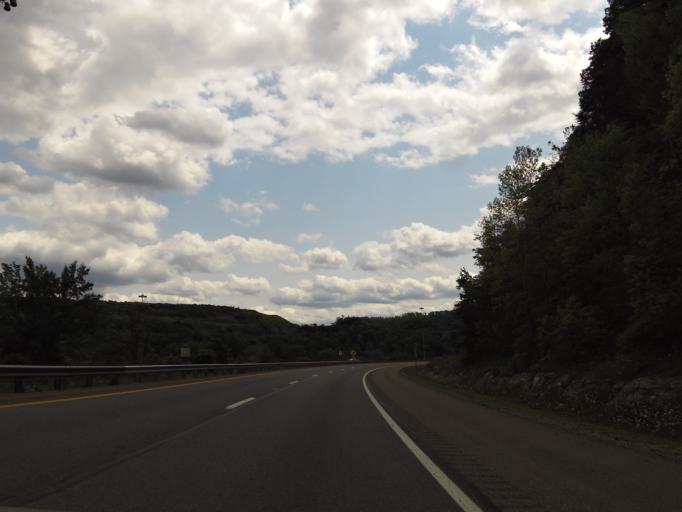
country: US
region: West Virginia
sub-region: Kanawha County
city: Charleston
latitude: 38.3766
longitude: -81.6068
